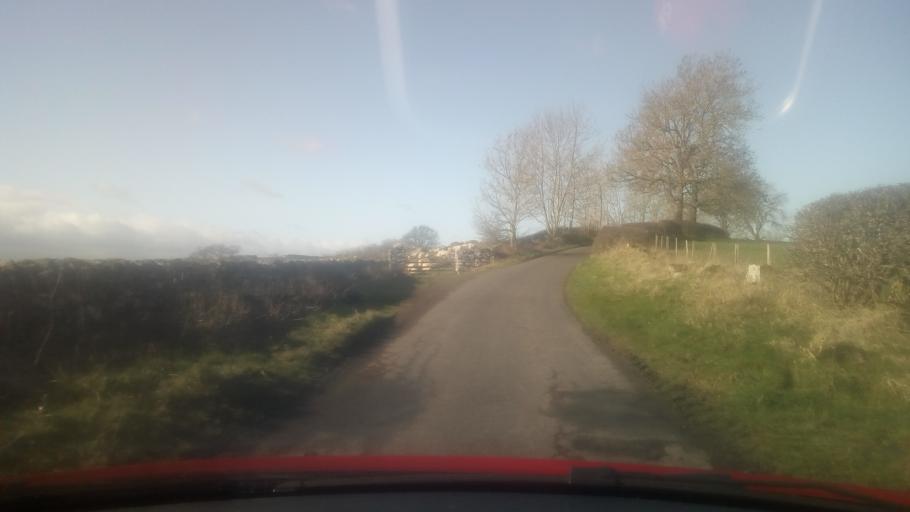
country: GB
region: Scotland
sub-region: The Scottish Borders
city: Jedburgh
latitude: 55.5216
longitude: -2.5983
